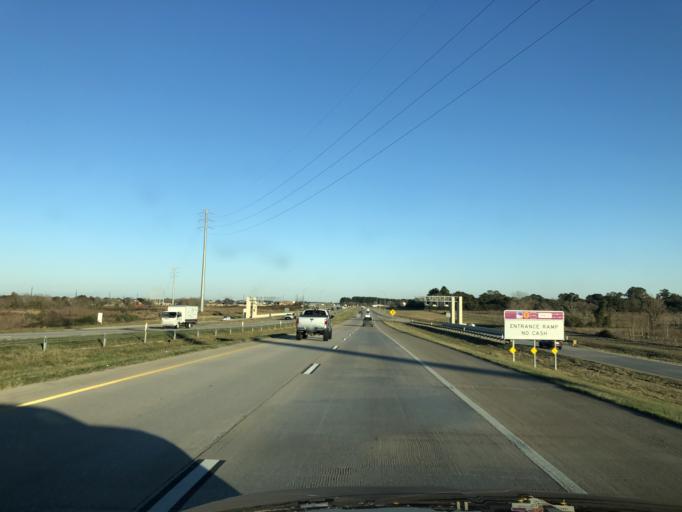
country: US
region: Texas
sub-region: Harris County
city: Cypress
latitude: 30.0534
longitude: -95.7326
